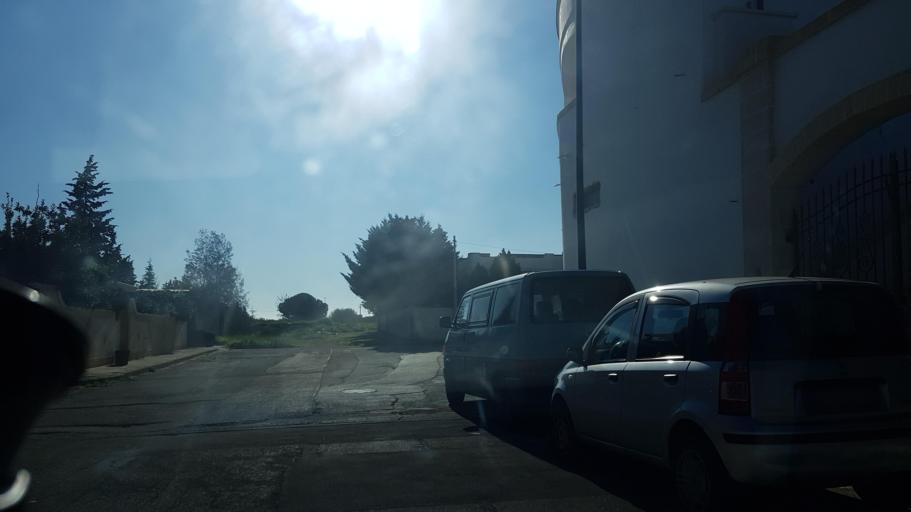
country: IT
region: Apulia
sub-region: Provincia di Lecce
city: Squinzano
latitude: 40.4290
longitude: 18.0472
